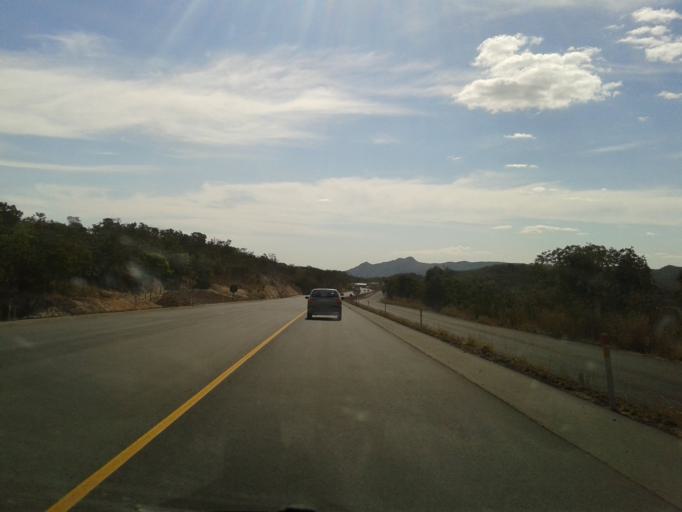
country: BR
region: Goias
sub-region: Goias
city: Goias
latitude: -15.9735
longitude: -50.1062
